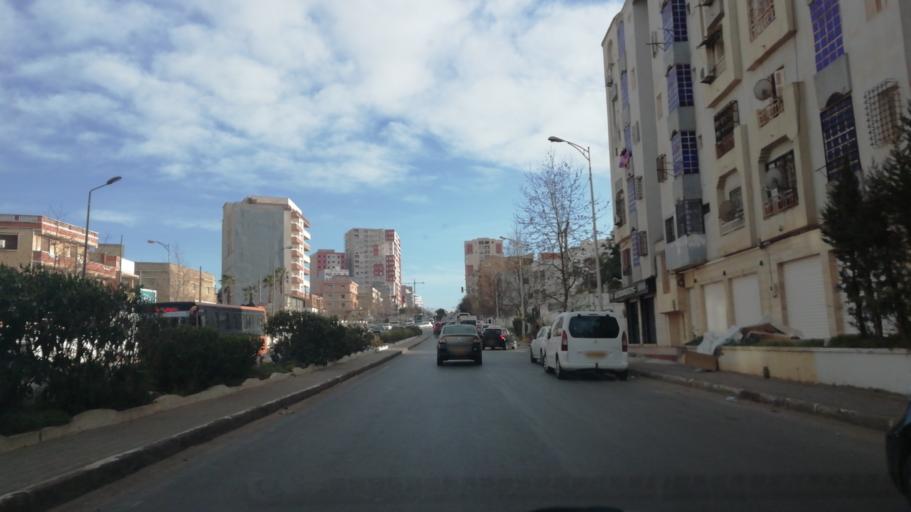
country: DZ
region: Oran
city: Bir el Djir
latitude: 35.7273
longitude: -0.5855
